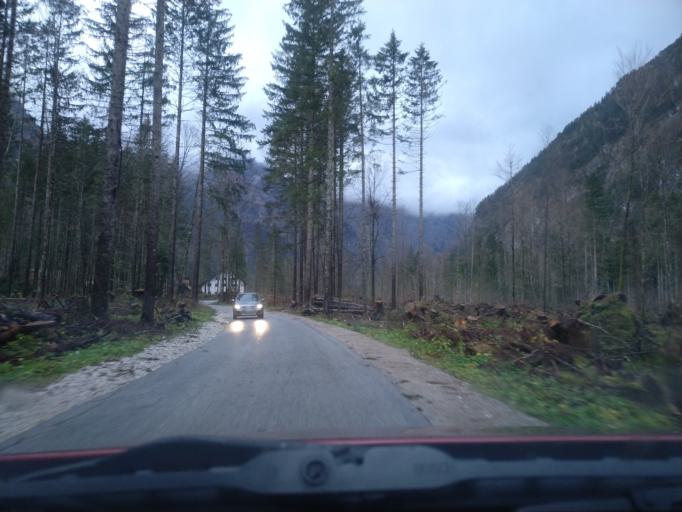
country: SI
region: Solcava
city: Solcava
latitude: 46.4007
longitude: 14.6312
